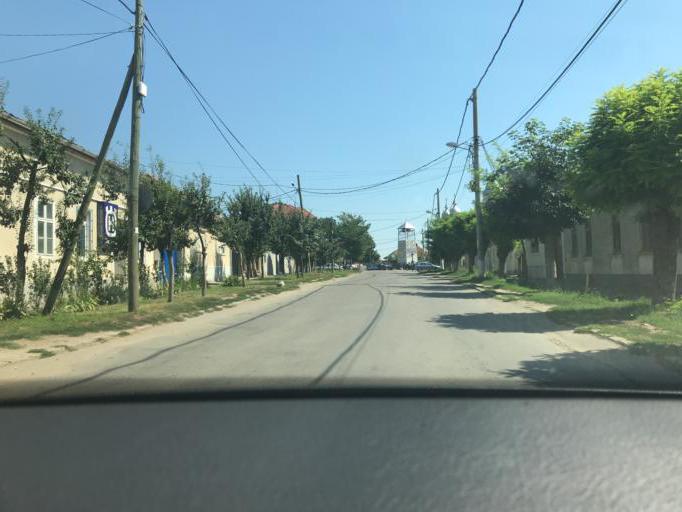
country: RO
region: Bihor
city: Margita
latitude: 47.3442
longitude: 22.3400
